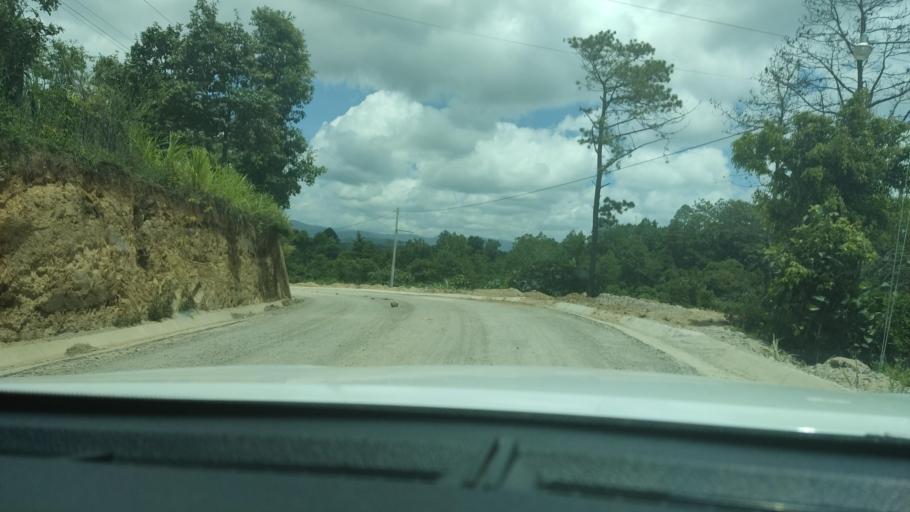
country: GT
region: Chimaltenango
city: San Martin Jilotepeque
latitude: 14.7918
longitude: -90.8054
